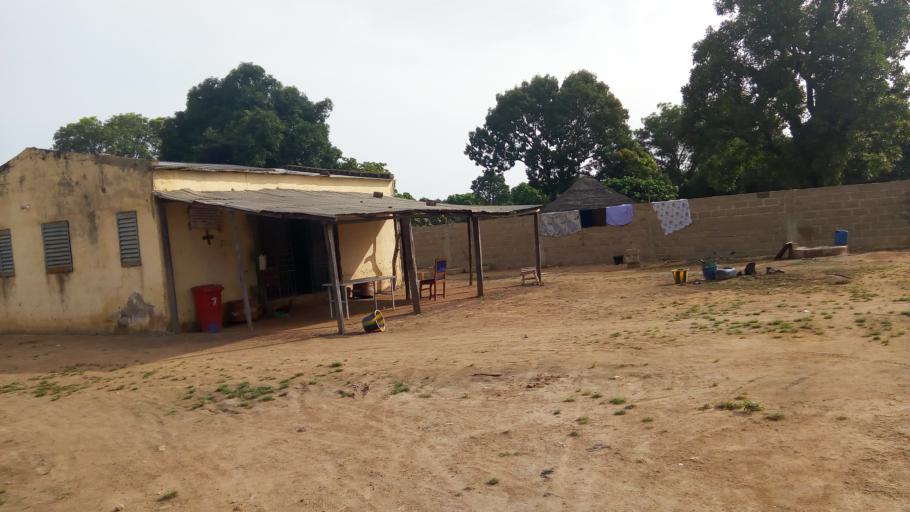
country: ML
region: Koulikoro
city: Kangaba
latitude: 11.6435
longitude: -8.7531
